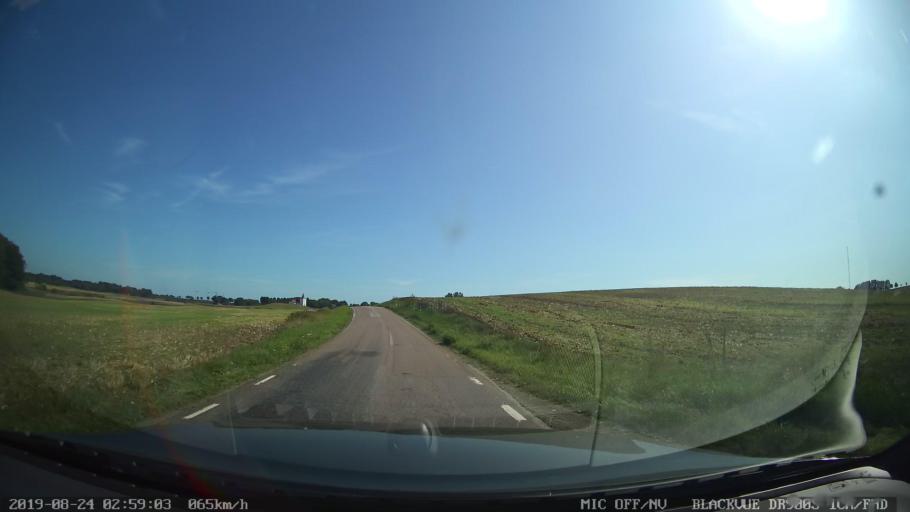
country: SE
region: Skane
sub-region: Skurups Kommun
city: Skurup
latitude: 55.4689
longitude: 13.4221
